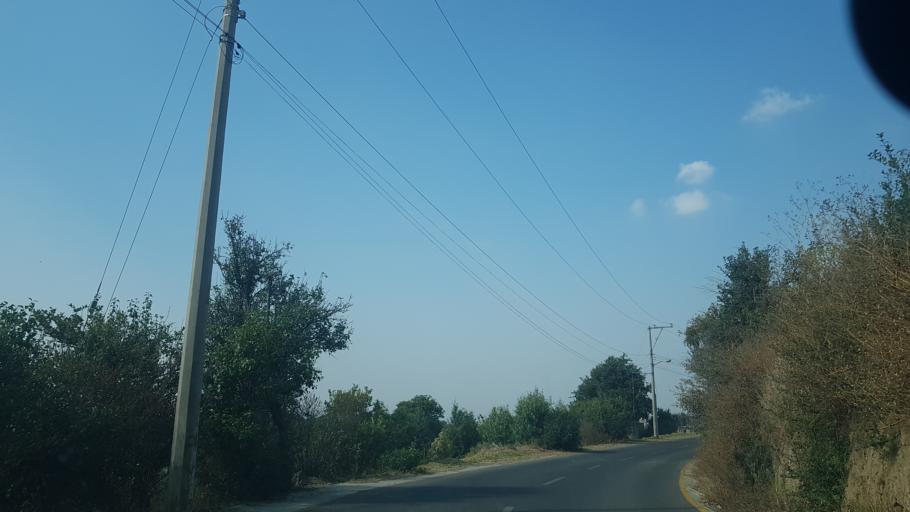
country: MX
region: Puebla
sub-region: Tochimilco
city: Santa Cruz Cuautomatitla
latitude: 18.8872
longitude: -98.6626
